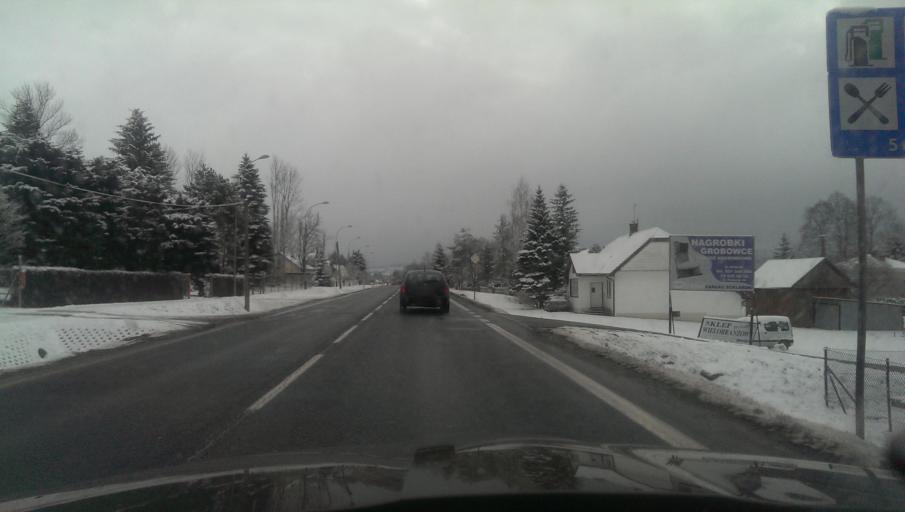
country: PL
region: Subcarpathian Voivodeship
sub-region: Powiat krosnienski
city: Miejsce Piastowe
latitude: 49.6109
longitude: 21.8023
